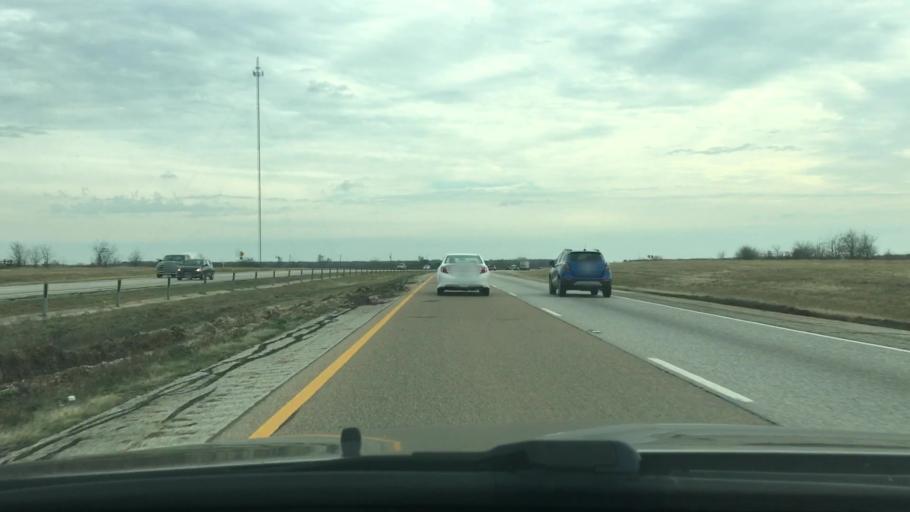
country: US
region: Texas
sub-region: Leon County
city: Centerville
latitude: 31.1071
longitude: -95.9666
